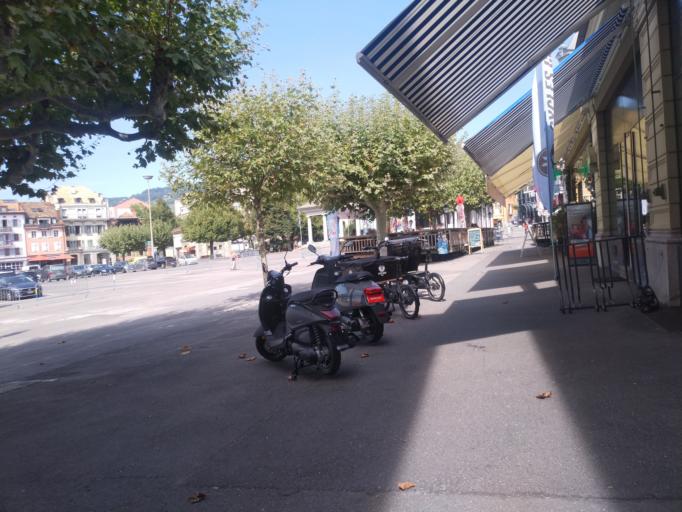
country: CH
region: Vaud
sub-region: Riviera-Pays-d'Enhaut District
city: Vevey
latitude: 46.4597
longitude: 6.8430
